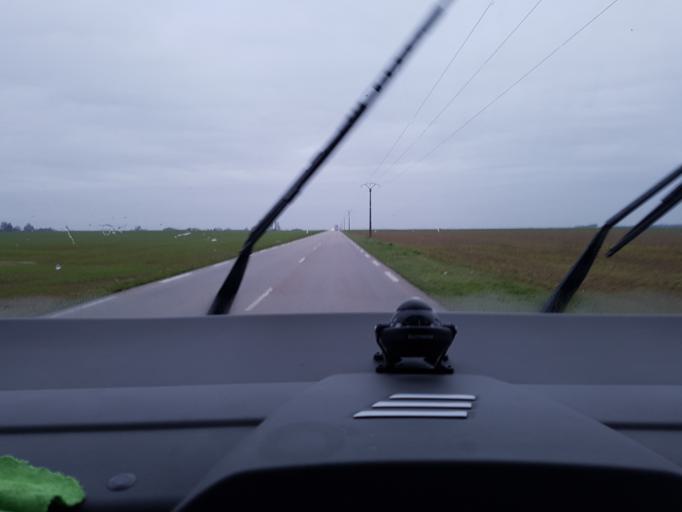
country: FR
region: Haute-Normandie
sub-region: Departement de l'Eure
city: Le Neubourg
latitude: 49.1533
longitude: 0.9829
